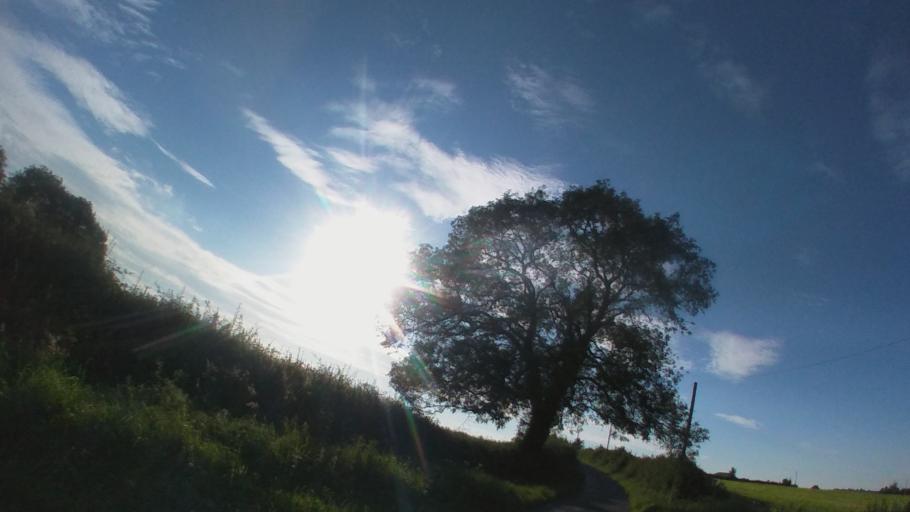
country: IE
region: Leinster
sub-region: Kilkenny
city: Kilkenny
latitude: 52.6952
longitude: -7.1931
